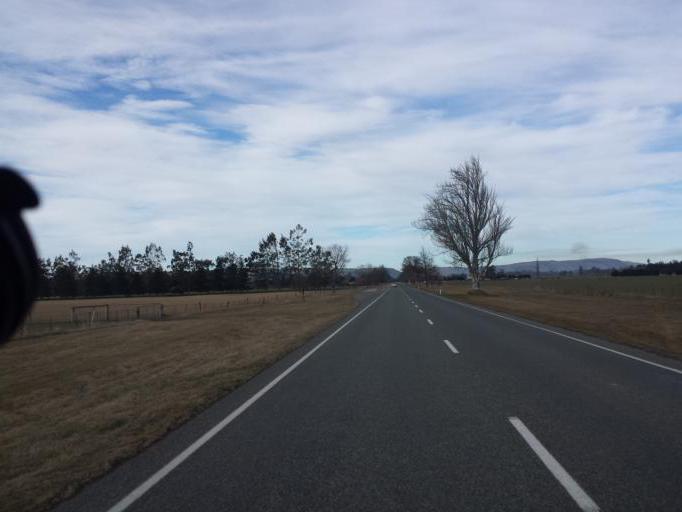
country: NZ
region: Canterbury
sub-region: Timaru District
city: Pleasant Point
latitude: -44.0697
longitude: 170.7901
